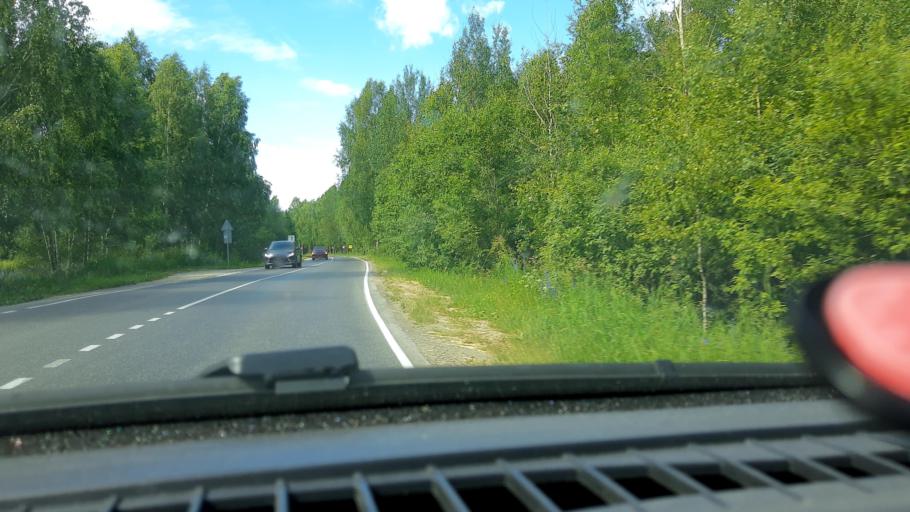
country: RU
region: Nizjnij Novgorod
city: Neklyudovo
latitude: 56.5002
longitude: 43.8511
